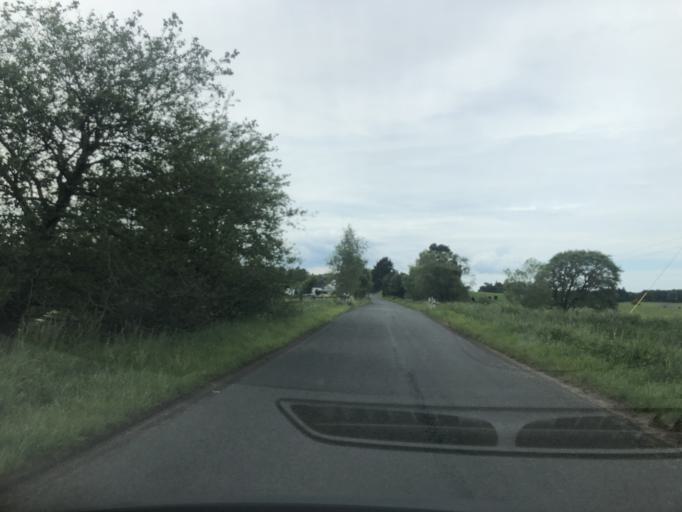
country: GB
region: Scotland
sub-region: The Scottish Borders
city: West Linton
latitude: 55.7315
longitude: -3.3258
